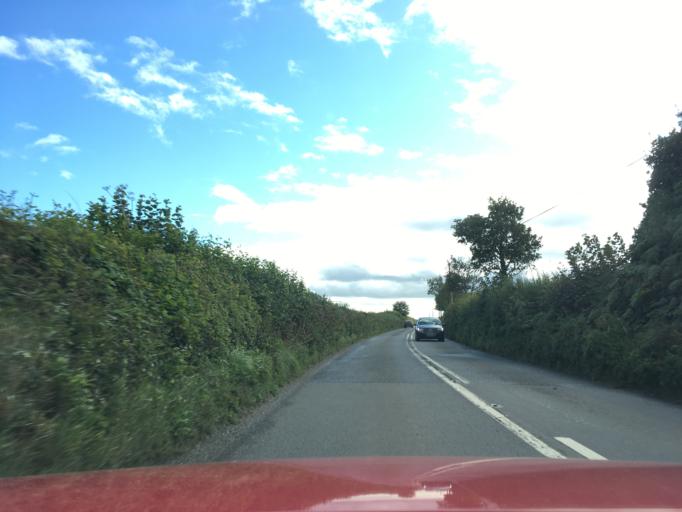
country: GB
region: England
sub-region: Devon
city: Kingsbridge
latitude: 50.3436
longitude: -3.7346
